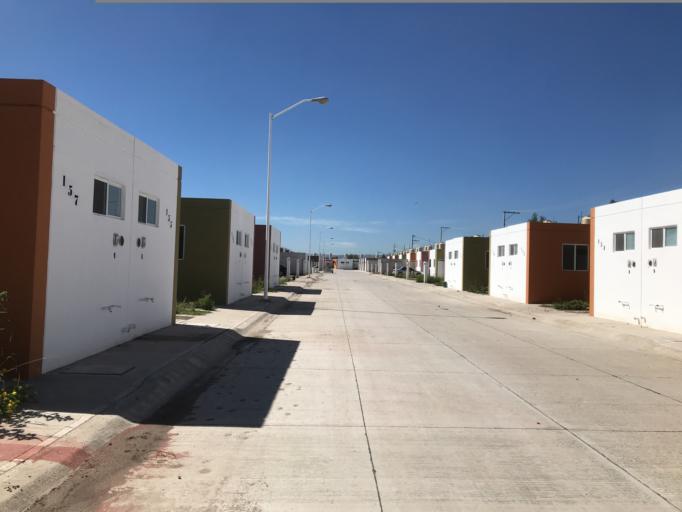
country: MX
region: Durango
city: Victoria de Durango
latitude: 24.0194
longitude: -104.5990
